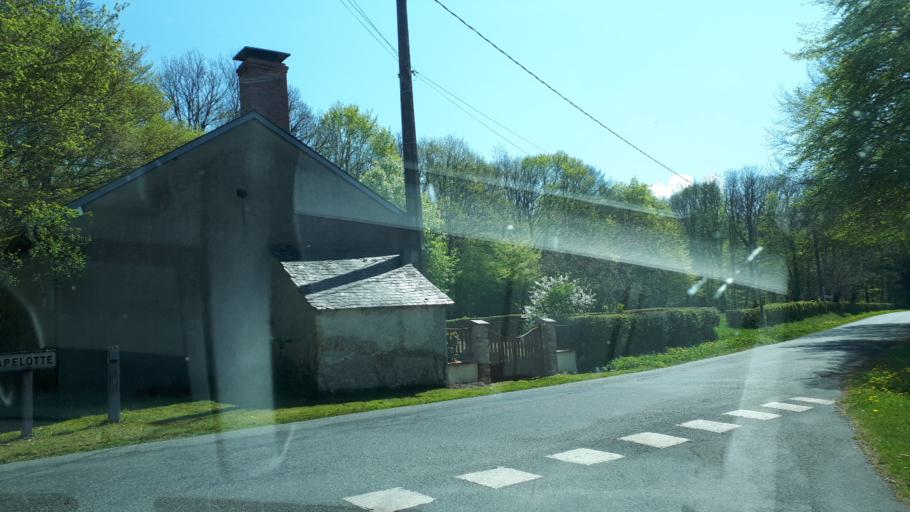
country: FR
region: Centre
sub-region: Departement du Cher
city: Henrichemont
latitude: 47.2974
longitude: 2.5798
